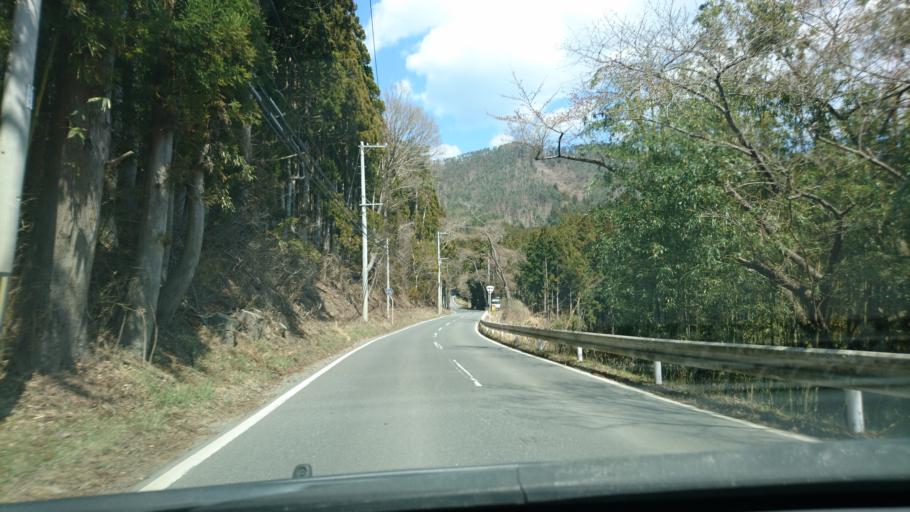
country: JP
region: Miyagi
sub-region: Oshika Gun
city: Onagawa Cho
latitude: 38.4431
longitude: 141.4738
